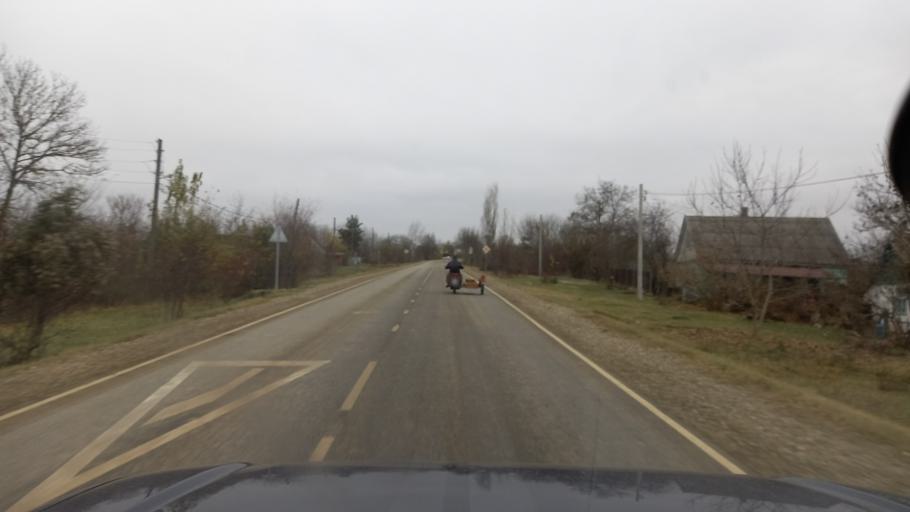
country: RU
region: Krasnodarskiy
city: Goryachiy Klyuch
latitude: 44.5252
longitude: 39.2923
